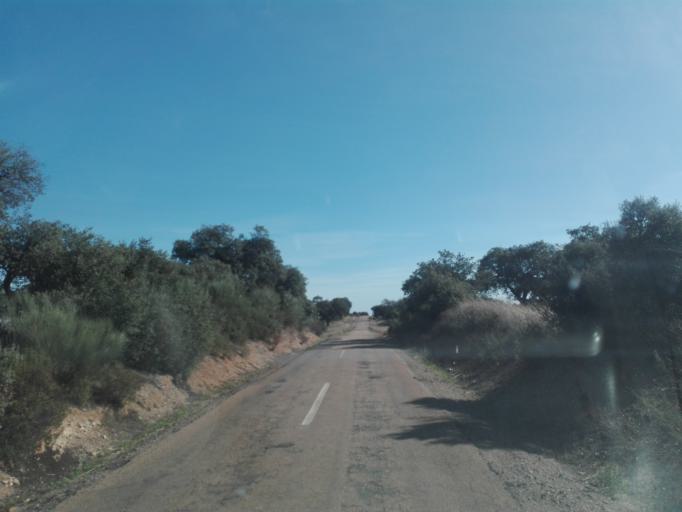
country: ES
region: Extremadura
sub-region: Provincia de Badajoz
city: Maguilla
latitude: 38.3404
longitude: -5.9141
